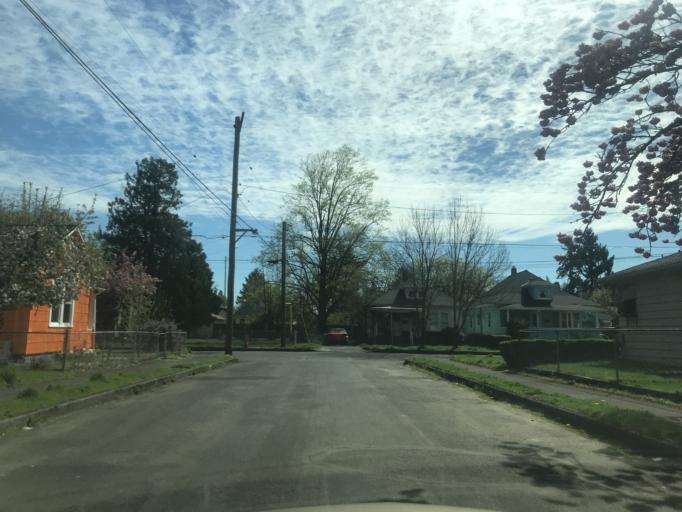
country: US
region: Oregon
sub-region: Multnomah County
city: Lents
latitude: 45.4842
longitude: -122.5937
